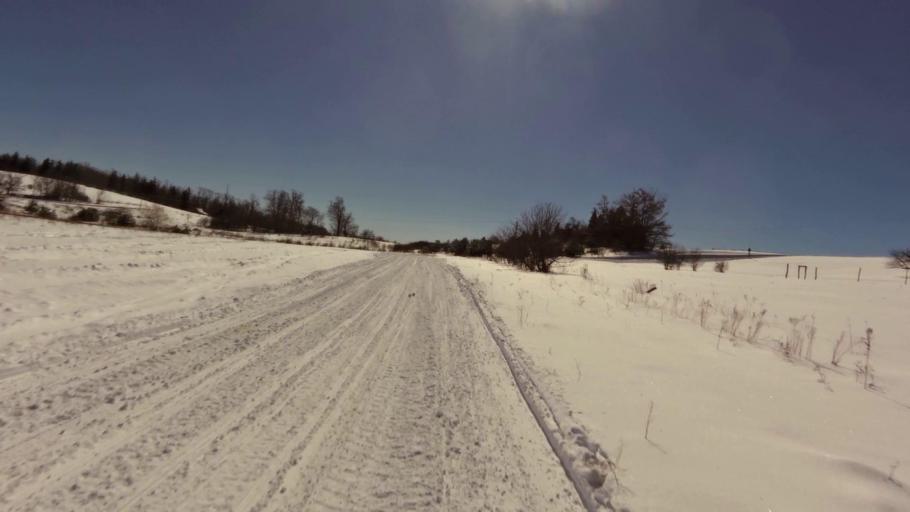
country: US
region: New York
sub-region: Chautauqua County
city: Mayville
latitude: 42.2183
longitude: -79.5182
